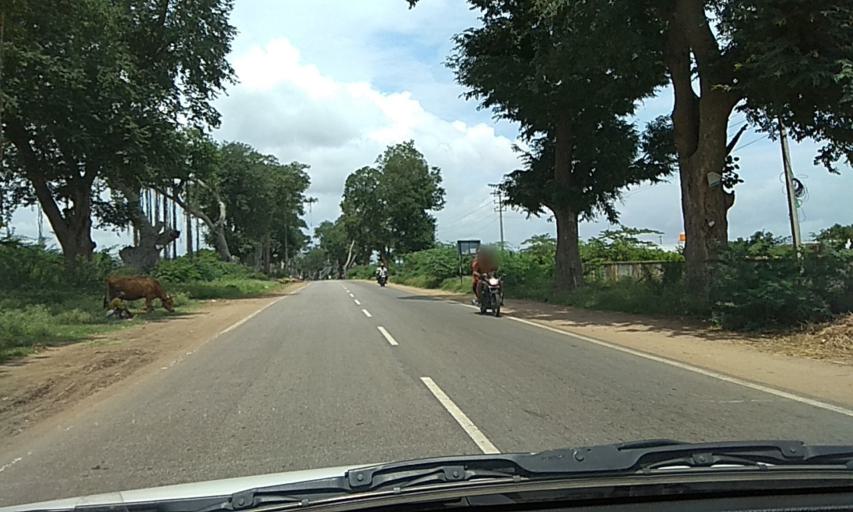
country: IN
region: Karnataka
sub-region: Chamrajnagar
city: Gundlupet
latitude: 11.8108
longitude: 76.7164
